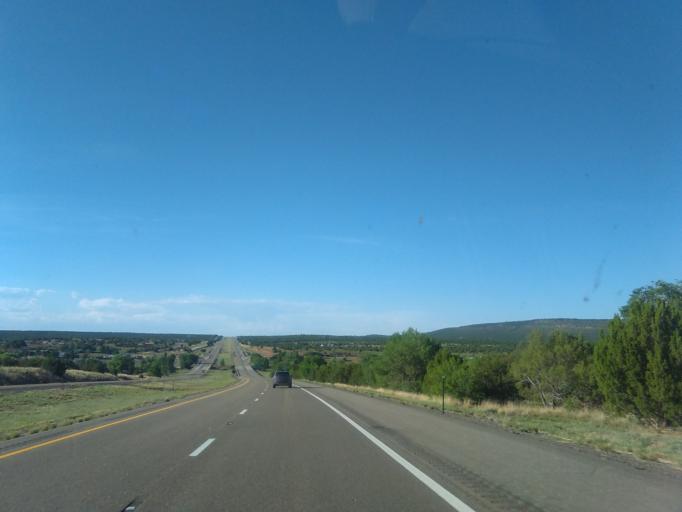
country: US
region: New Mexico
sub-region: San Miguel County
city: Las Vegas
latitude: 35.4528
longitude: -105.2783
